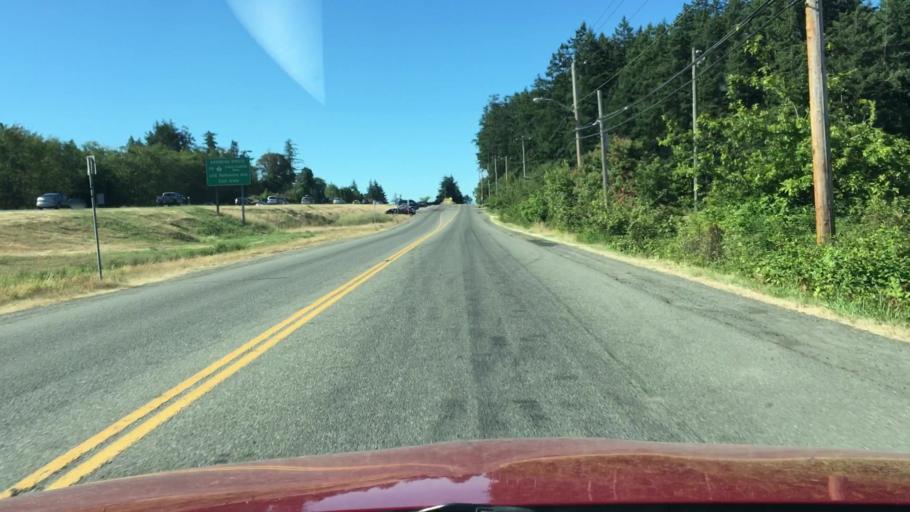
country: CA
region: British Columbia
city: Victoria
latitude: 48.5109
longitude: -123.3845
